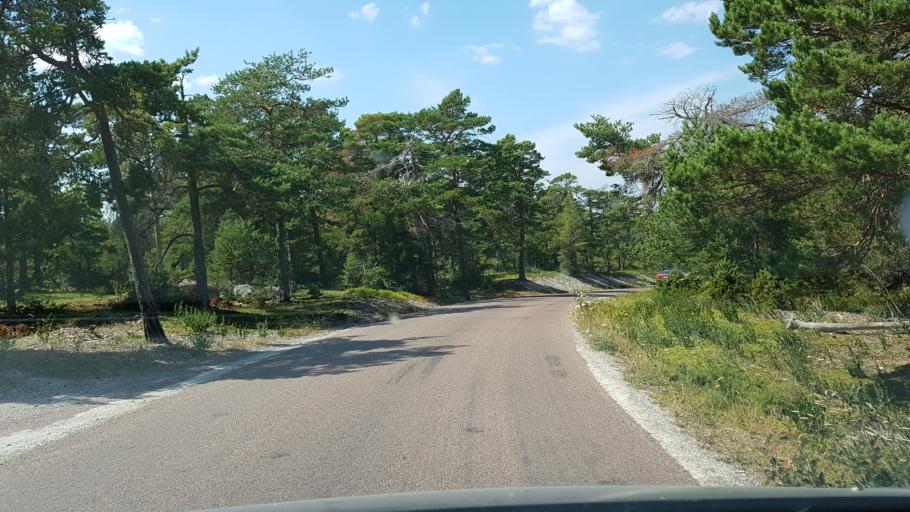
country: SE
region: Gotland
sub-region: Gotland
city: Visby
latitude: 57.6848
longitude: 18.3565
